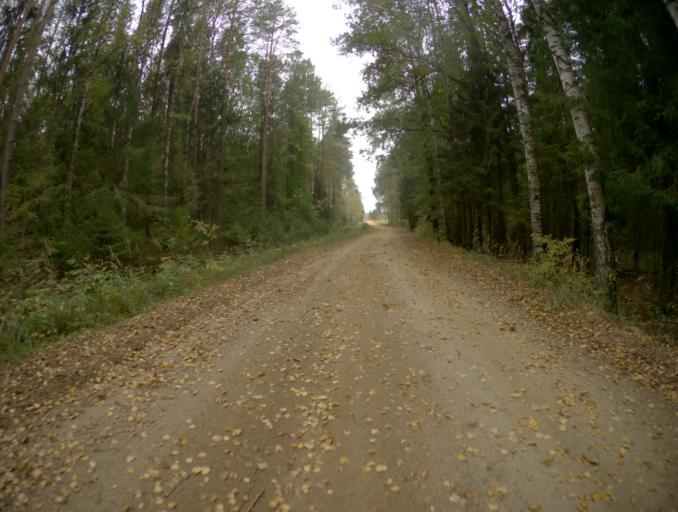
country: RU
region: Vladimir
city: Kideksha
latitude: 56.4718
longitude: 40.7202
